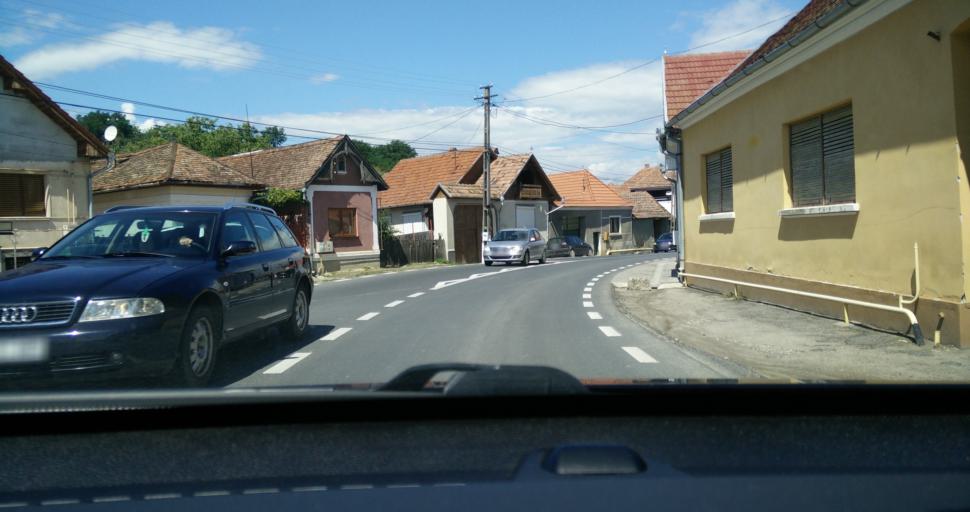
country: RO
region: Alba
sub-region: Comuna Sasciori
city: Sebesel
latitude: 45.8878
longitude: 23.5640
